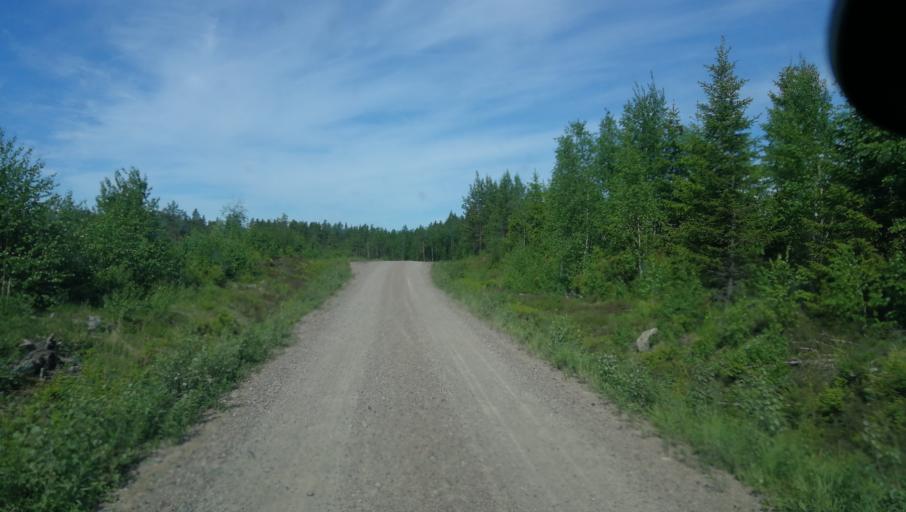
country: SE
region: Dalarna
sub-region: Vansbro Kommun
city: Vansbro
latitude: 60.8208
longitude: 14.1722
